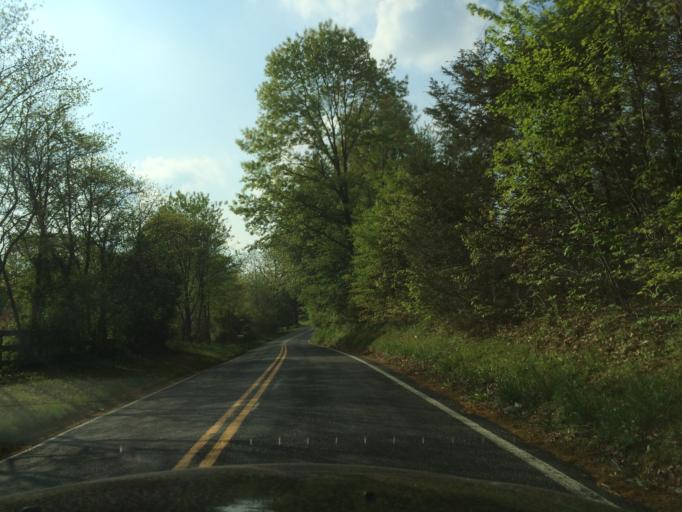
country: US
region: Maryland
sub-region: Carroll County
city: Mount Airy
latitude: 39.3028
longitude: -77.0987
